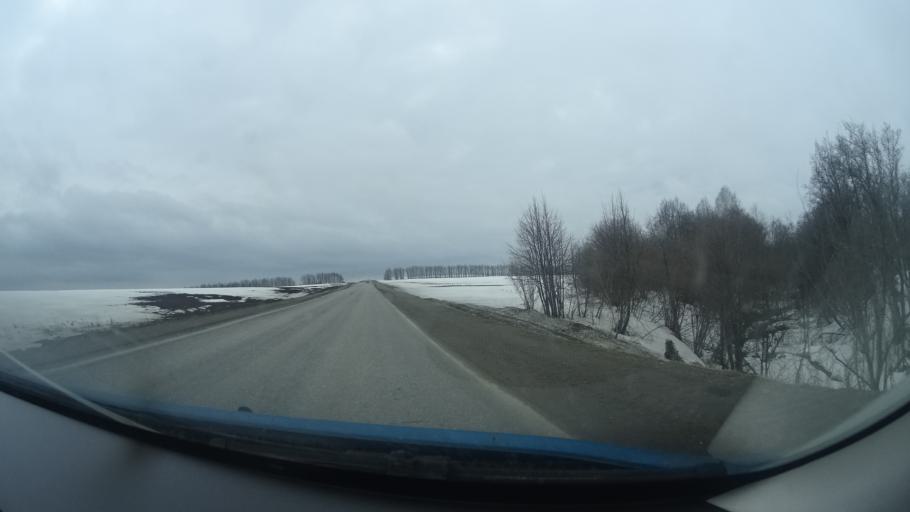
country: RU
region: Bashkortostan
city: Birsk
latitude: 55.3627
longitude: 55.5797
